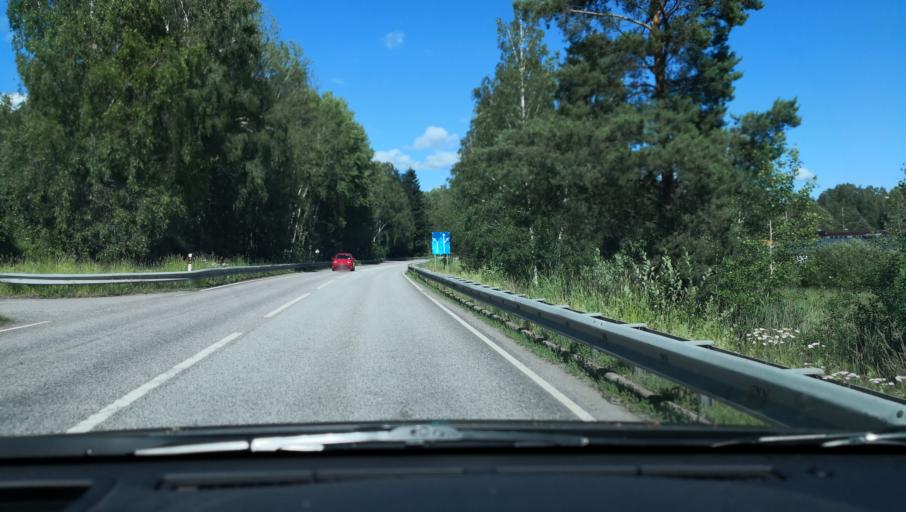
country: SE
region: Soedermanland
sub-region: Eskilstuna Kommun
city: Skogstorp
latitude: 59.3269
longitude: 16.4203
